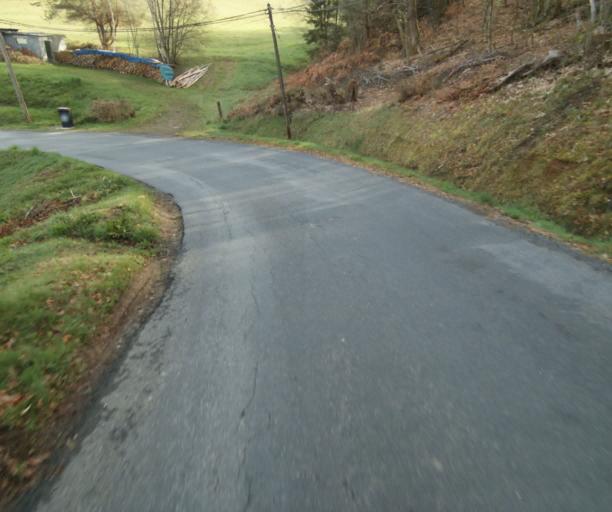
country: FR
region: Limousin
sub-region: Departement de la Correze
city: Naves
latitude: 45.3346
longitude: 1.8241
